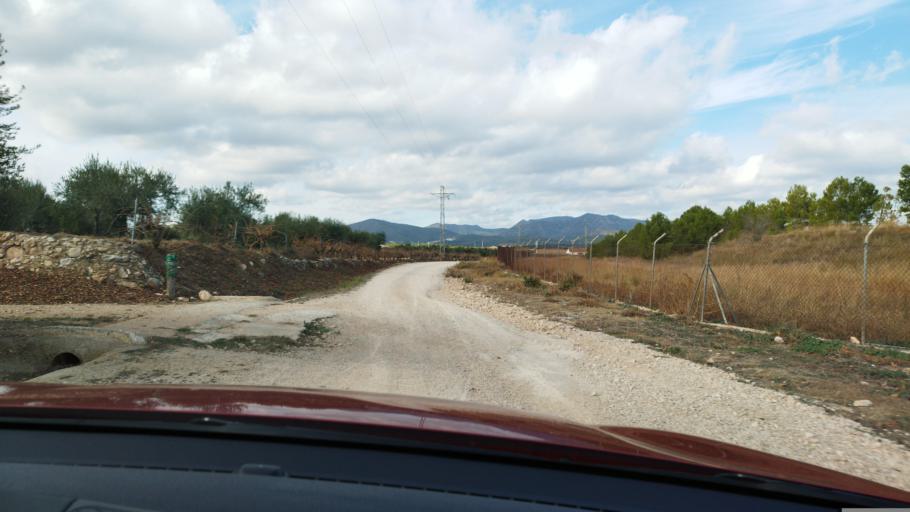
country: ES
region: Catalonia
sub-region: Provincia de Tarragona
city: Albinyana
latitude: 41.2615
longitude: 1.5008
